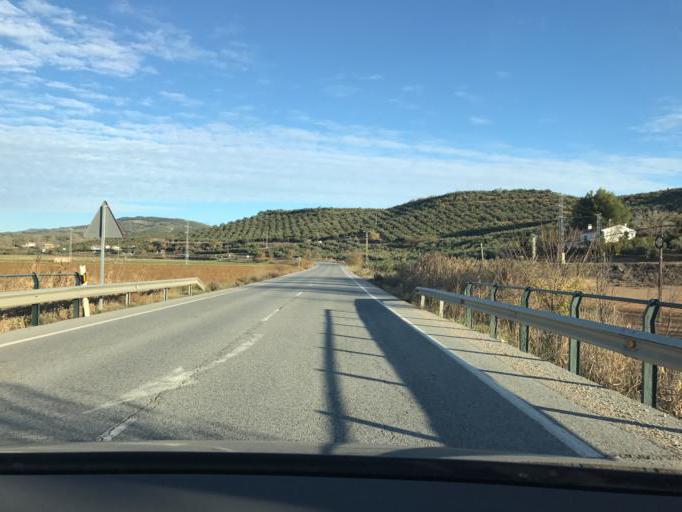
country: ES
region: Andalusia
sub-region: Provincia de Granada
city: Iznalloz
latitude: 37.4060
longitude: -3.5078
